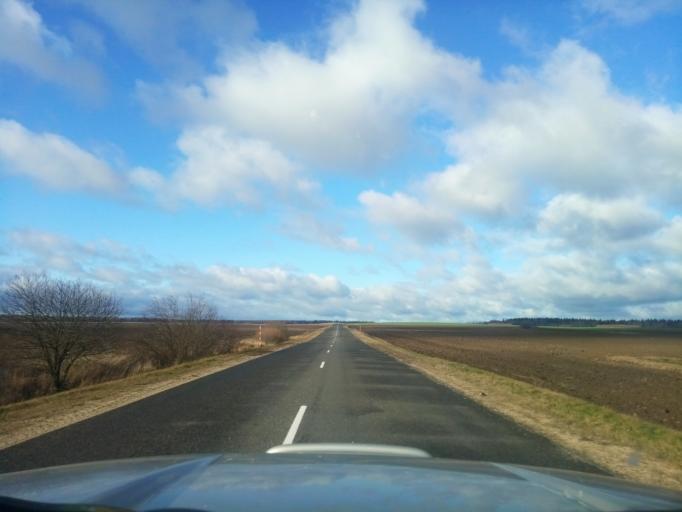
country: BY
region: Minsk
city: Kapyl'
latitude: 53.1642
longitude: 27.0650
